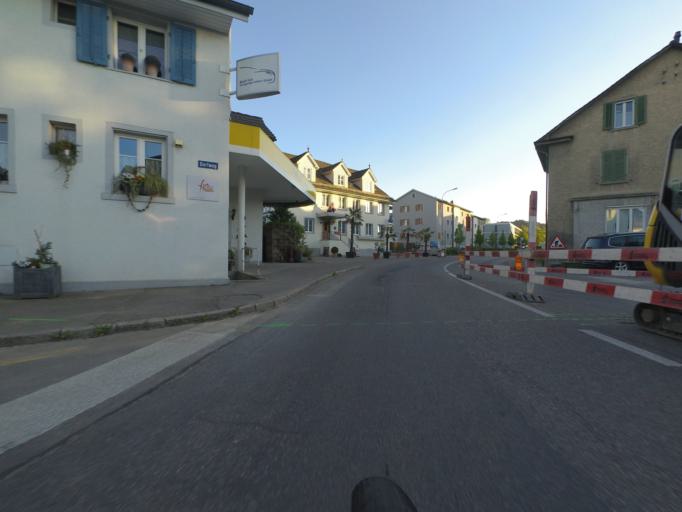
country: CH
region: Thurgau
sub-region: Frauenfeld District
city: Gachnang
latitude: 47.5449
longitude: 8.8414
